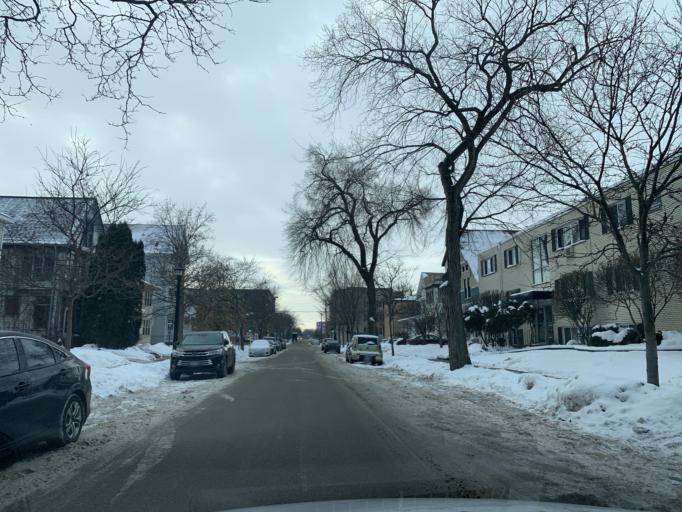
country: US
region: Minnesota
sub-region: Hennepin County
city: Minneapolis
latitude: 44.9529
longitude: -93.2932
